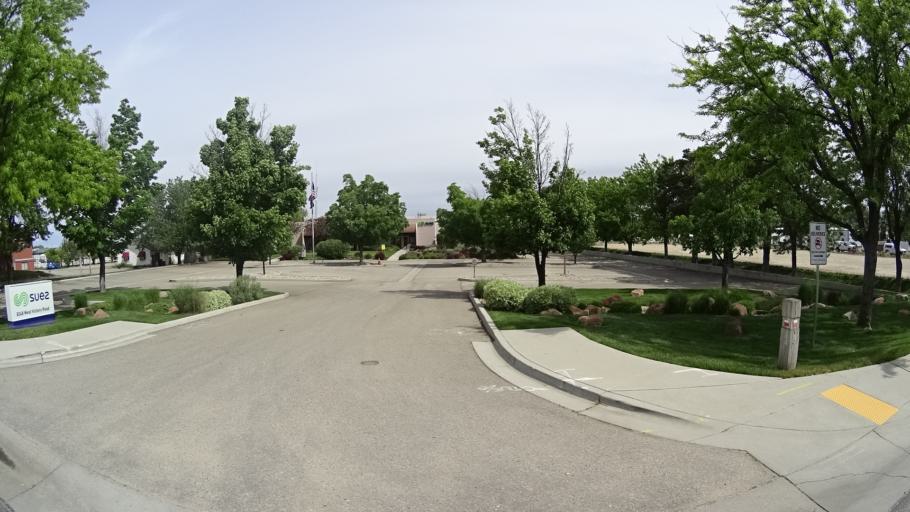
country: US
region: Idaho
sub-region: Ada County
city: Garden City
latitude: 43.5757
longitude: -116.2835
